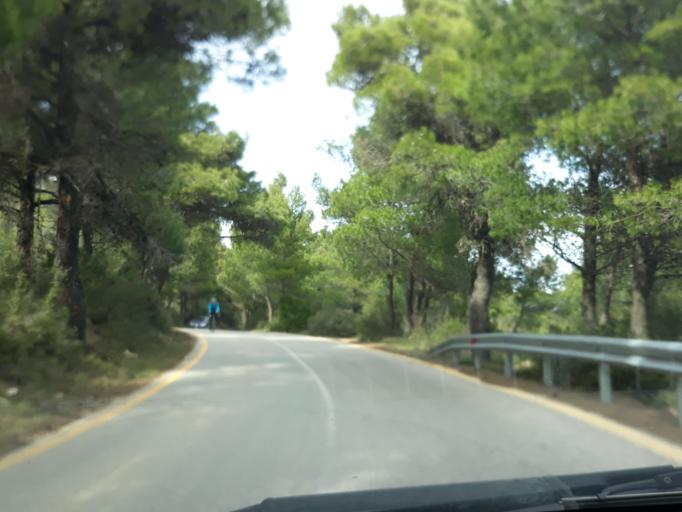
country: GR
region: Attica
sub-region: Nomarchia Anatolikis Attikis
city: Varybobi
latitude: 38.1736
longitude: 23.7910
